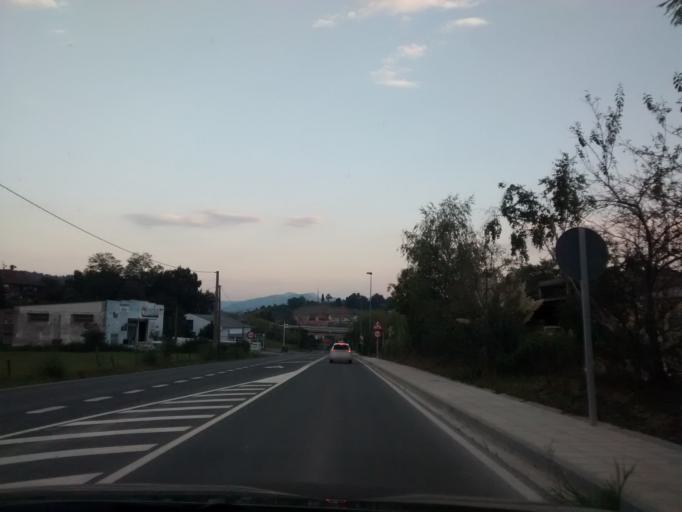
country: ES
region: Cantabria
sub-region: Provincia de Cantabria
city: Lierganes
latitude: 43.3873
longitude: -3.7462
